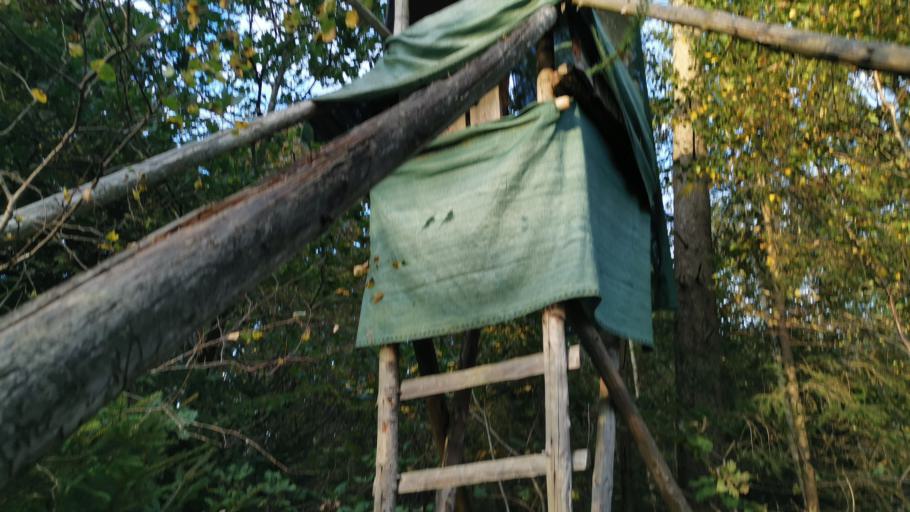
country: DE
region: Bavaria
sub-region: Upper Bavaria
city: Pullach im Isartal
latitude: 48.0759
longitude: 11.5617
